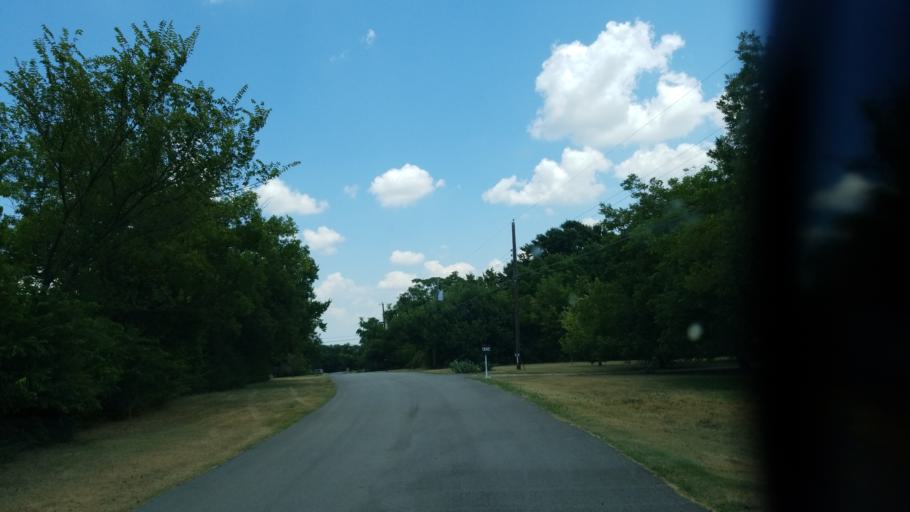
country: US
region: Texas
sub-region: Dallas County
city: Duncanville
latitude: 32.6723
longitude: -96.8905
